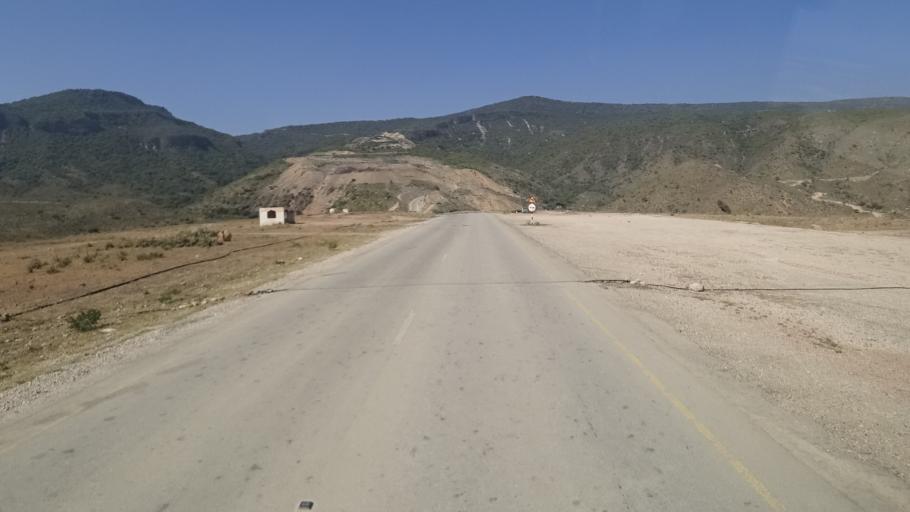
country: OM
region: Zufar
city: Salalah
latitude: 17.0385
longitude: 54.6130
